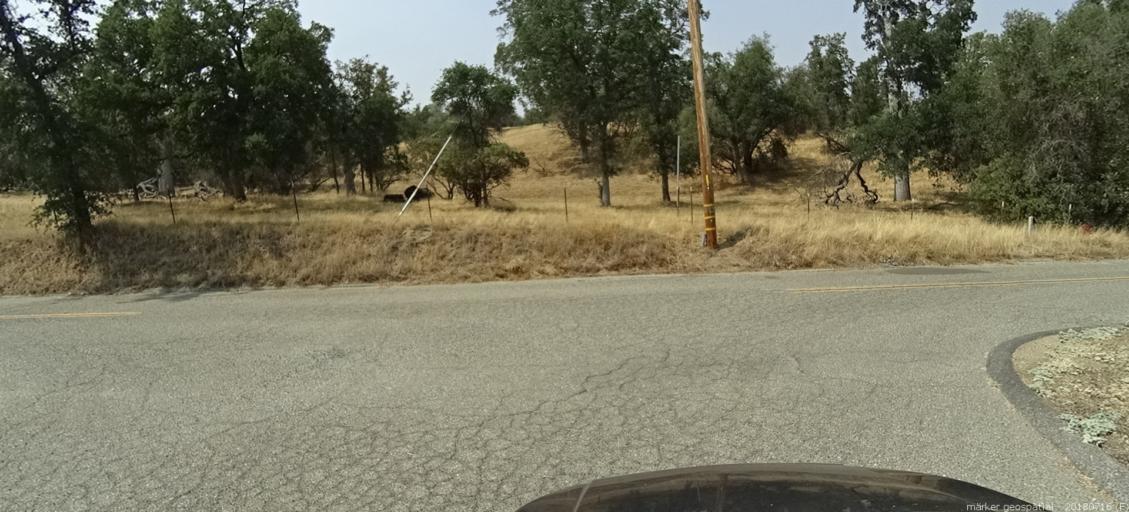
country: US
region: California
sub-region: Madera County
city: Yosemite Lakes
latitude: 37.2195
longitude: -119.7812
